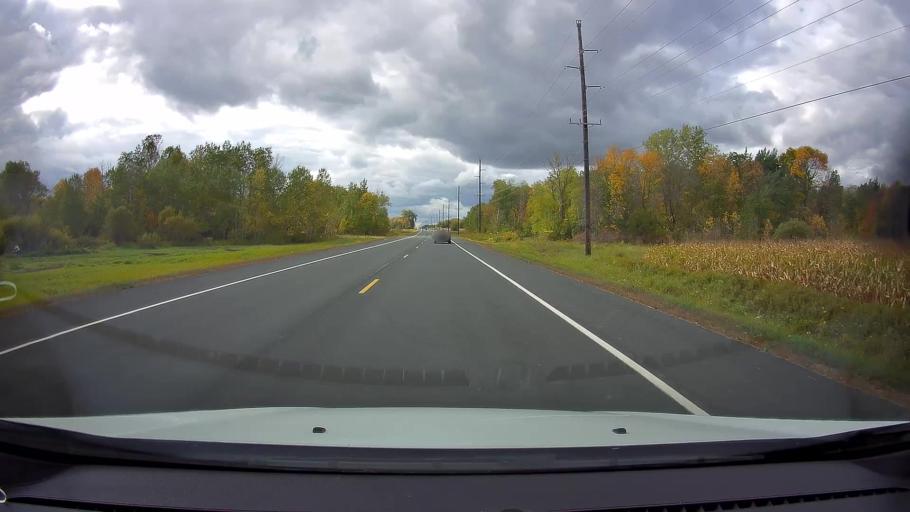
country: US
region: Minnesota
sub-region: Chisago County
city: Shafer
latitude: 45.3973
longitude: -92.7323
